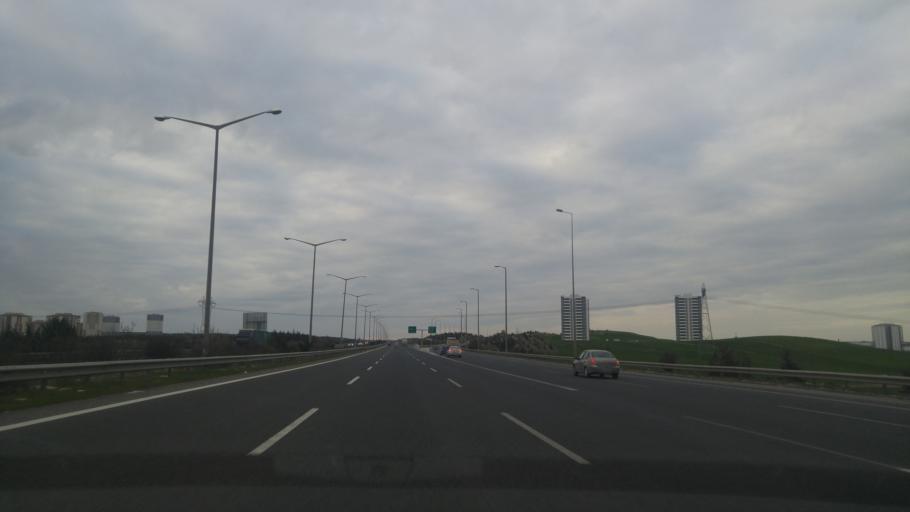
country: TR
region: Ankara
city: Etimesgut
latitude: 40.0046
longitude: 32.6340
